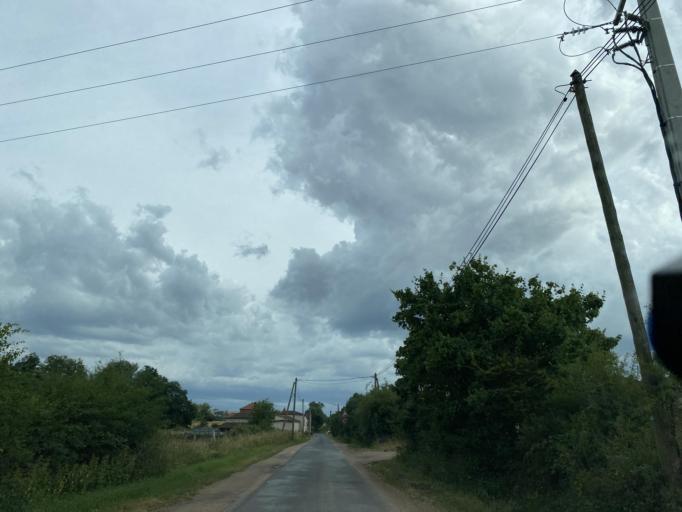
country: FR
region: Auvergne
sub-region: Departement du Puy-de-Dome
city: Courpiere
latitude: 45.7430
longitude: 3.4542
